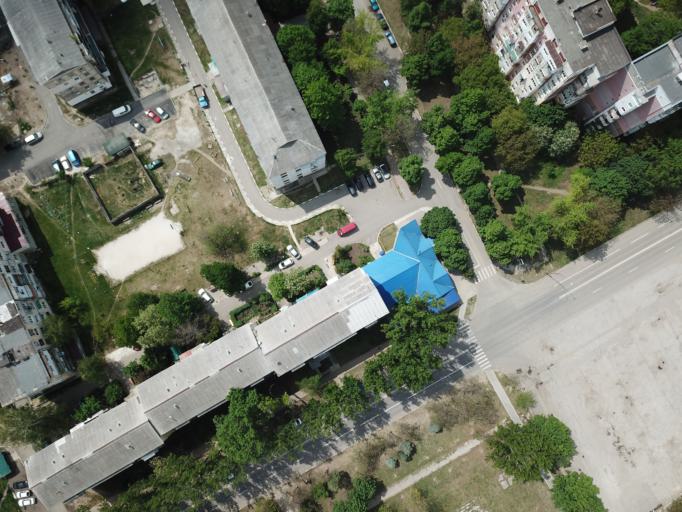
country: MD
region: Ungheni
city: Ungheni
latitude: 47.2211
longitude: 27.7984
